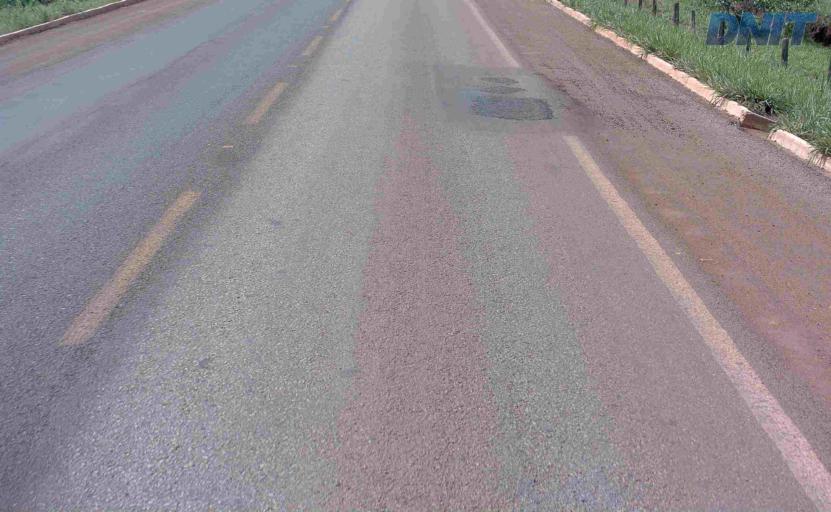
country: BR
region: Goias
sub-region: Barro Alto
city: Barro Alto
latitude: -14.9721
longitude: -48.9303
